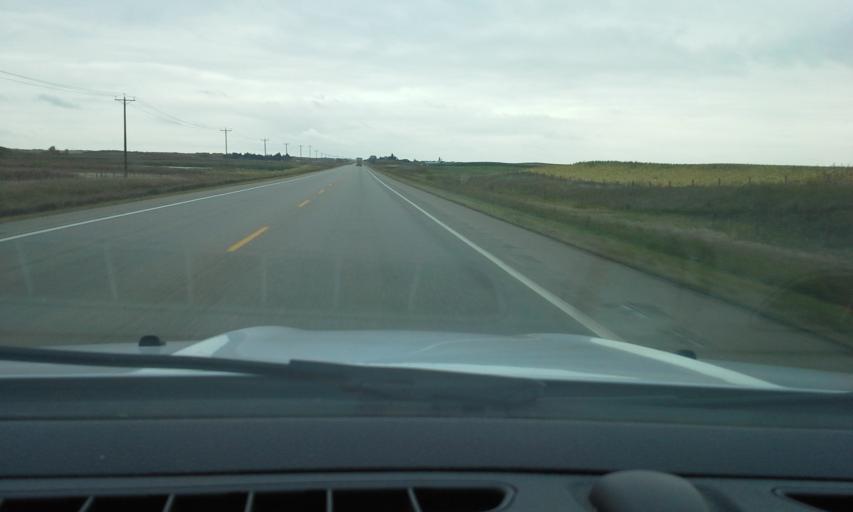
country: CA
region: Saskatchewan
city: Lloydminster
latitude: 53.2780
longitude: -109.8773
